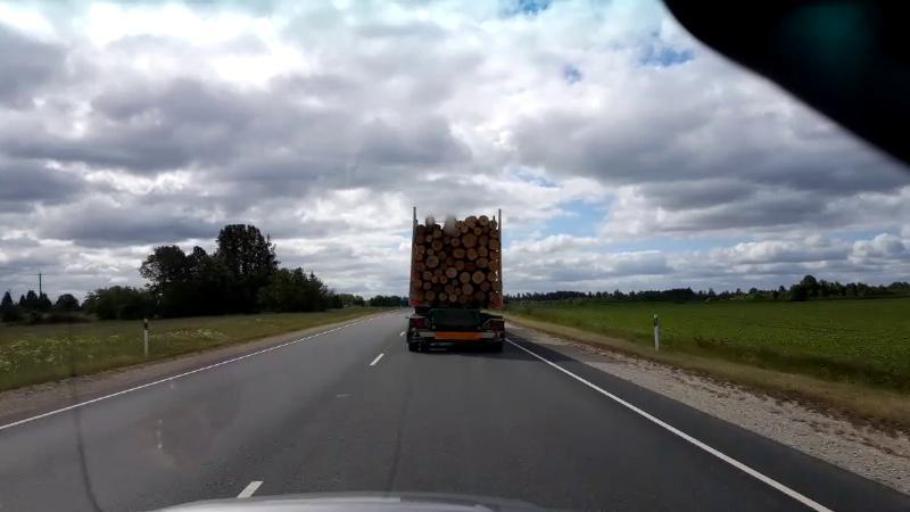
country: EE
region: Paernumaa
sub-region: Halinga vald
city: Parnu-Jaagupi
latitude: 58.6939
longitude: 24.4325
